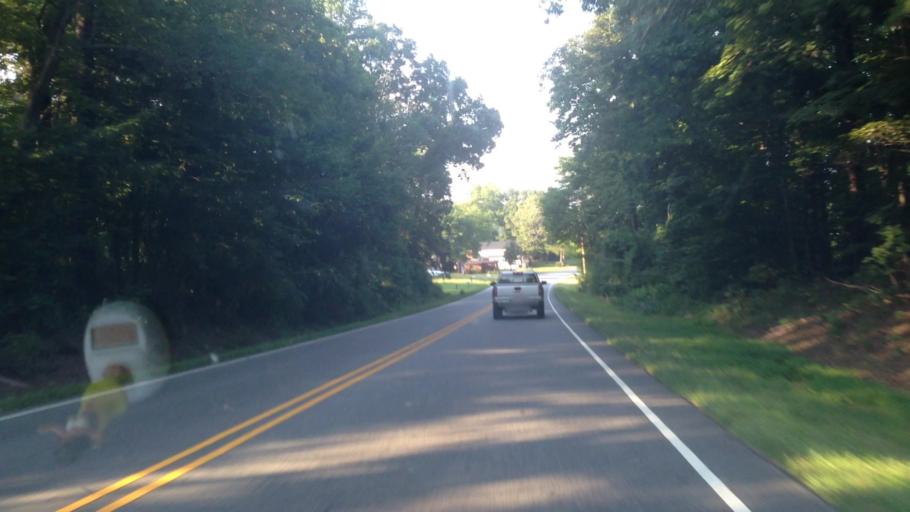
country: US
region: North Carolina
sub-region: Rockingham County
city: Reidsville
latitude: 36.2818
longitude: -79.7574
